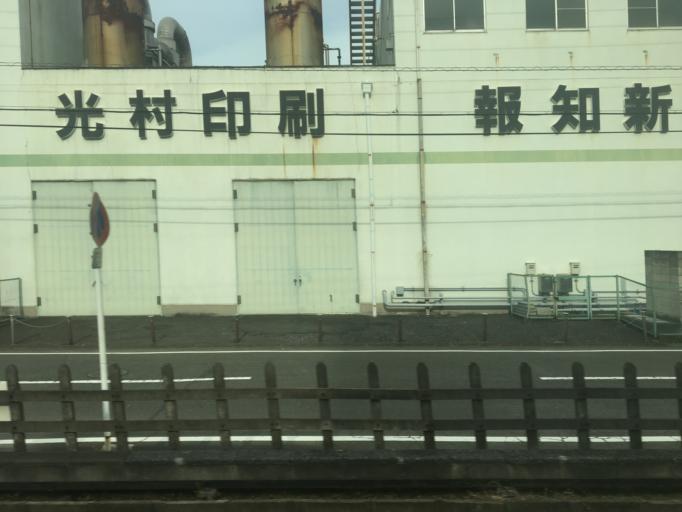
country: JP
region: Saitama
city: Kawagoe
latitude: 35.8872
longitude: 139.4508
